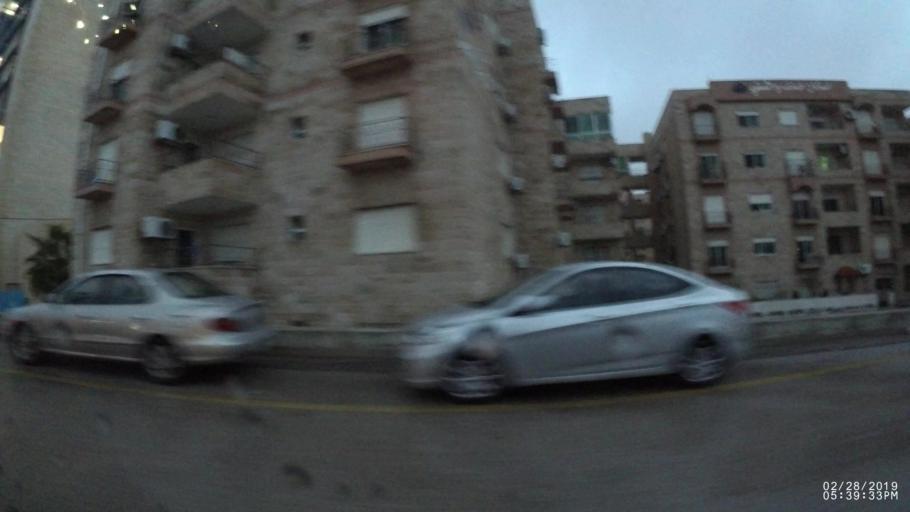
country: JO
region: Amman
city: Al Jubayhah
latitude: 32.0033
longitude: 35.8761
